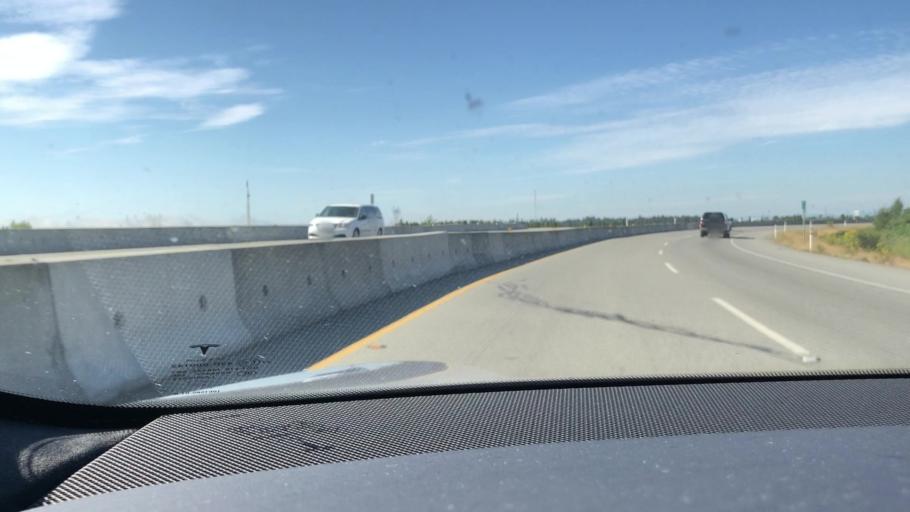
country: CA
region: British Columbia
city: Ladner
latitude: 49.1287
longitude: -123.0140
